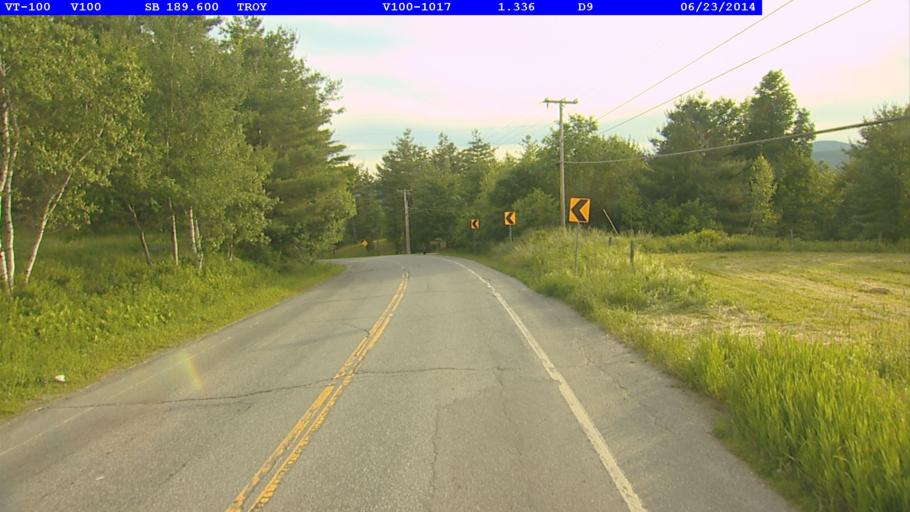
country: US
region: Vermont
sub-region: Orleans County
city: Newport
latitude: 44.9092
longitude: -72.3885
